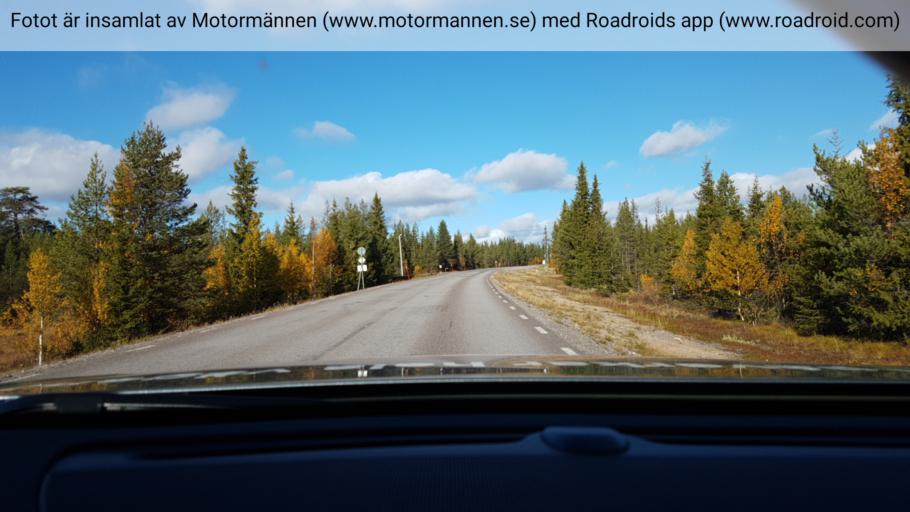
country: SE
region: Norrbotten
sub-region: Arjeplogs Kommun
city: Arjeplog
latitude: 65.8927
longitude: 18.3686
